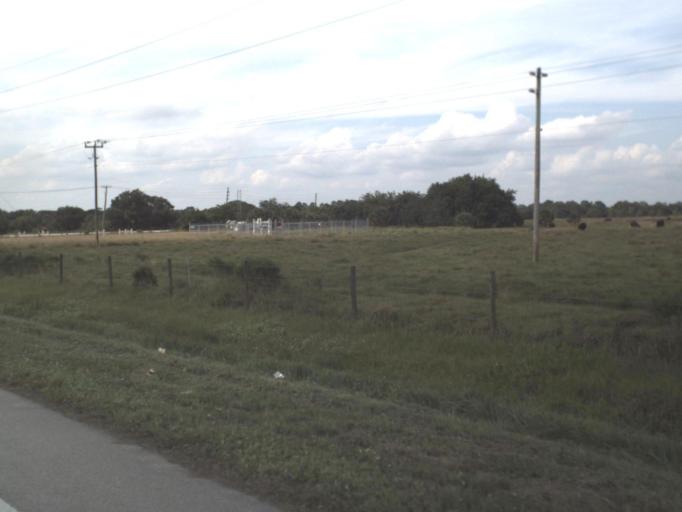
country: US
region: Florida
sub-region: Okeechobee County
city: Taylor Creek
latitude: 27.1694
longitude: -80.6930
